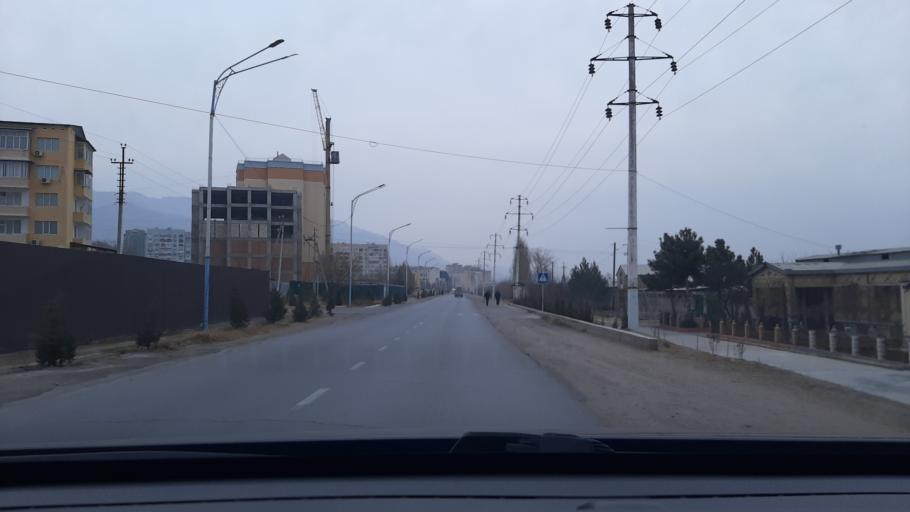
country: TJ
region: Viloyati Sughd
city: Khujand
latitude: 40.2821
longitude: 69.5864
